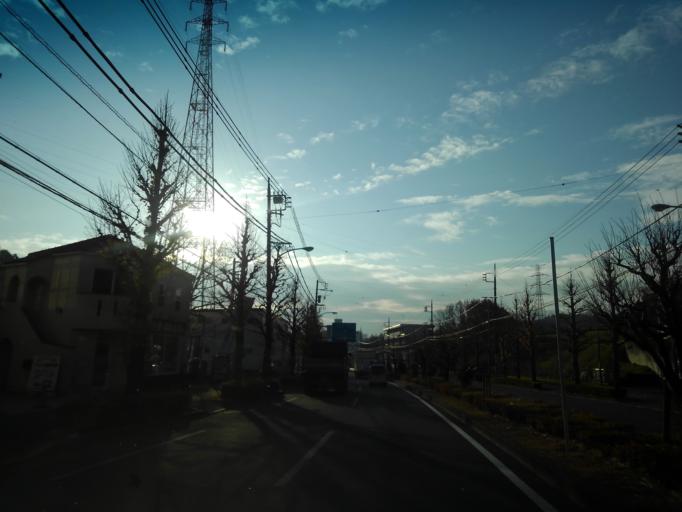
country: JP
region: Tokyo
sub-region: Machida-shi
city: Machida
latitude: 35.5963
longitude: 139.4473
